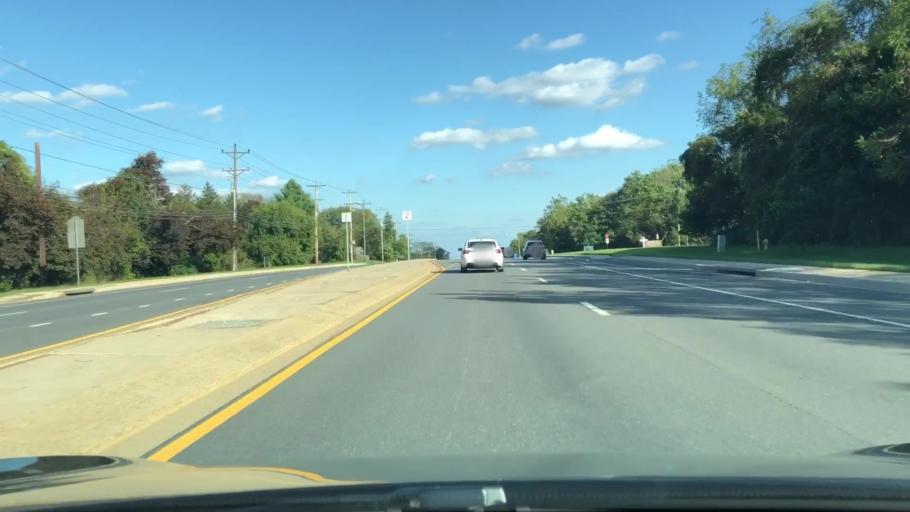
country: US
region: Delaware
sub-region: New Castle County
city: Bellefonte
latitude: 39.8271
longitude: -75.5157
